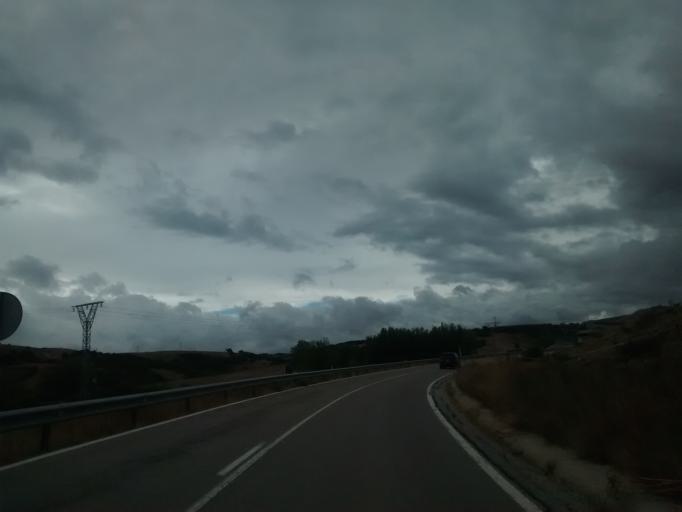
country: ES
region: Cantabria
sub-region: Provincia de Cantabria
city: Mataporquera
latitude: 42.8788
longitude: -4.0696
